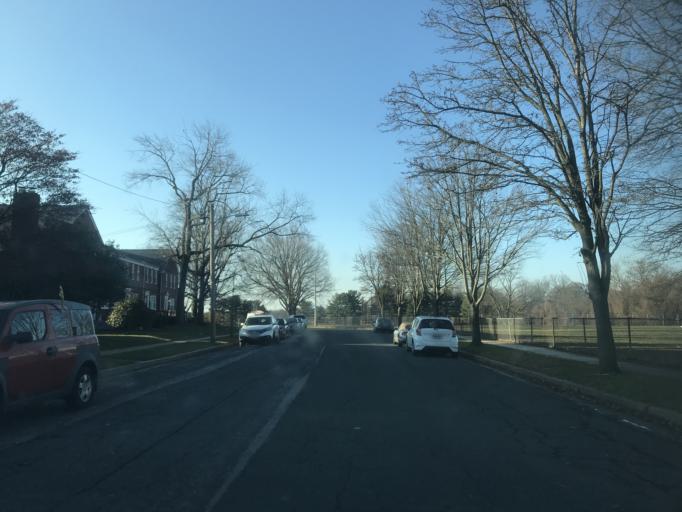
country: US
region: Maryland
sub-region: Baltimore County
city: Towson
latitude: 39.3895
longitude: -76.5767
